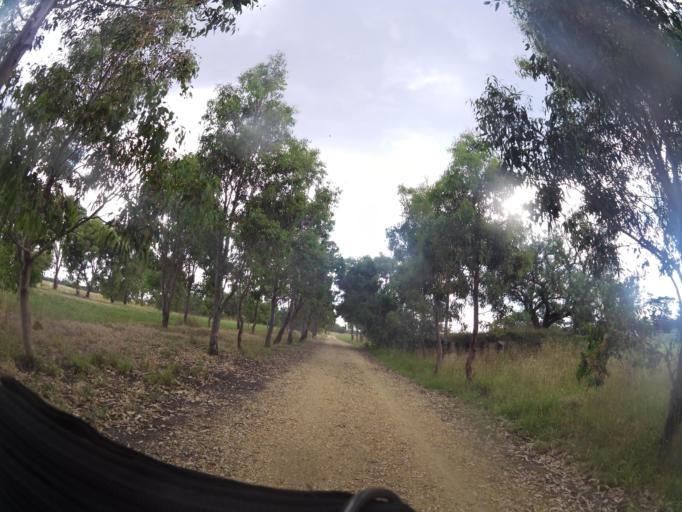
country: AU
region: Victoria
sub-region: Wellington
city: Heyfield
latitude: -38.0147
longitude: 146.6919
